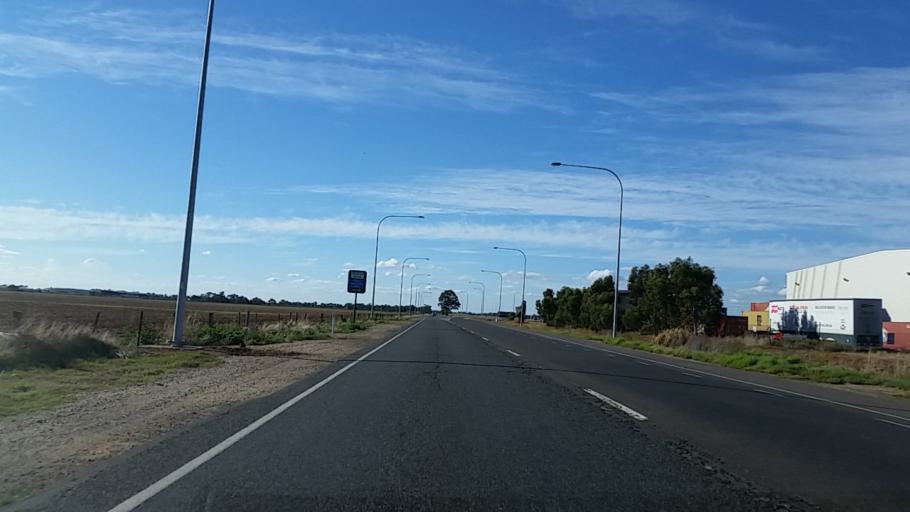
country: AU
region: South Australia
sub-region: Salisbury
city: Salisbury
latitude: -34.7185
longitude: 138.5995
